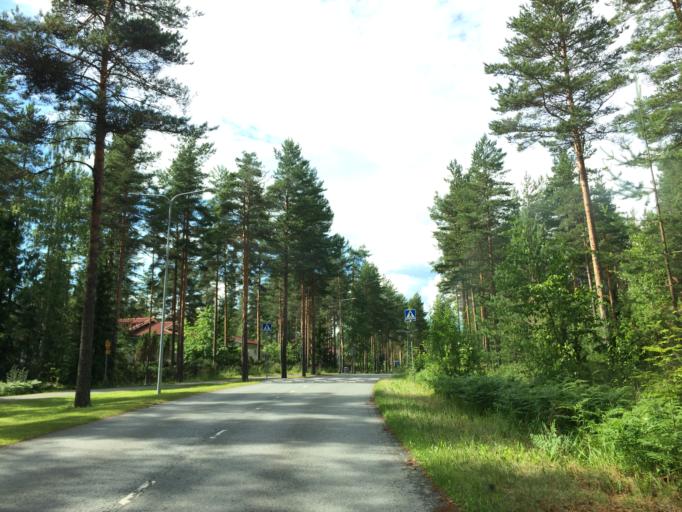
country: FI
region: Haeme
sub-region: Haemeenlinna
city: Turenki
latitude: 60.9373
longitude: 24.6490
